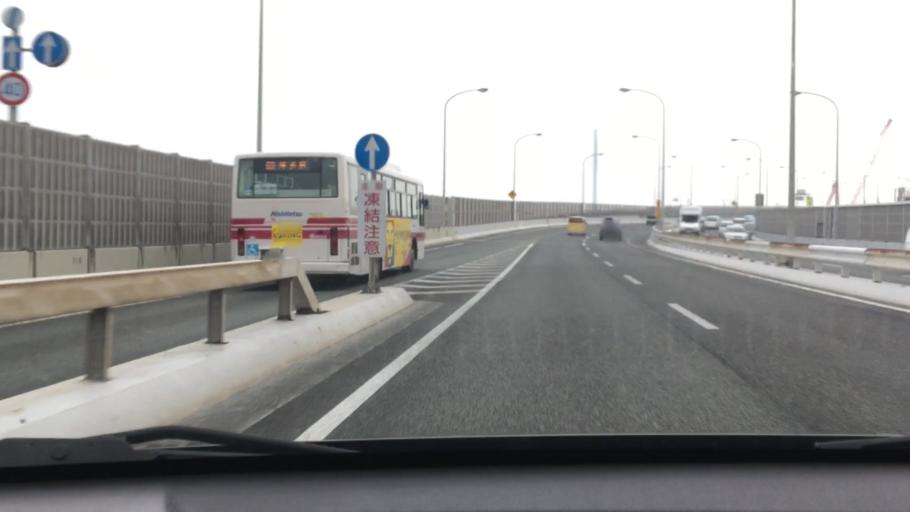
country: JP
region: Fukuoka
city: Fukuoka-shi
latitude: 33.6002
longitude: 130.3759
